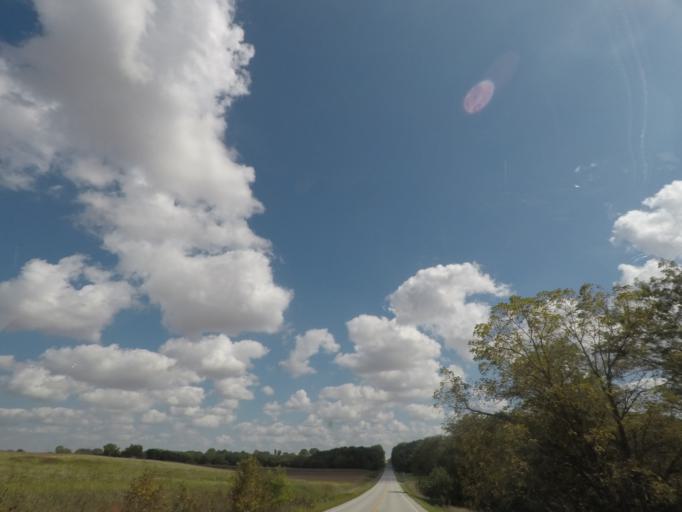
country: US
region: Iowa
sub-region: Story County
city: Nevada
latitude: 42.0777
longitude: -93.3619
